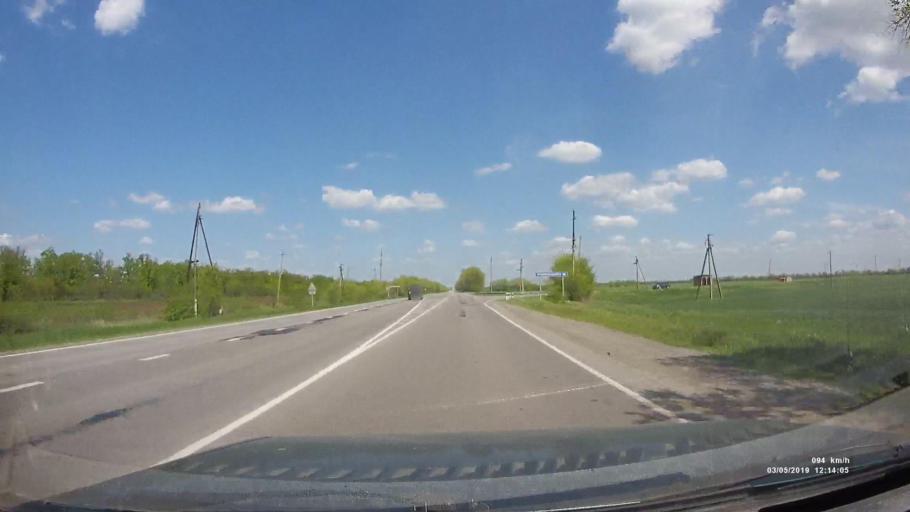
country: RU
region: Rostov
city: Melikhovskaya
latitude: 47.3393
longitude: 40.5599
